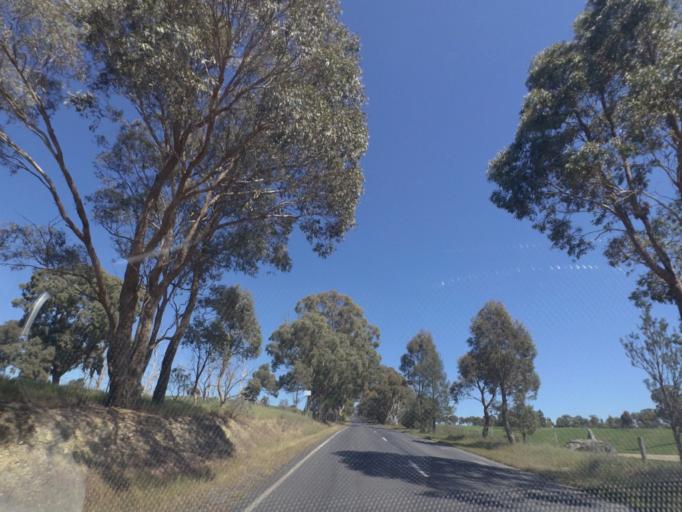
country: AU
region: Victoria
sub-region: Whittlesea
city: Whittlesea
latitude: -37.2658
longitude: 145.0502
